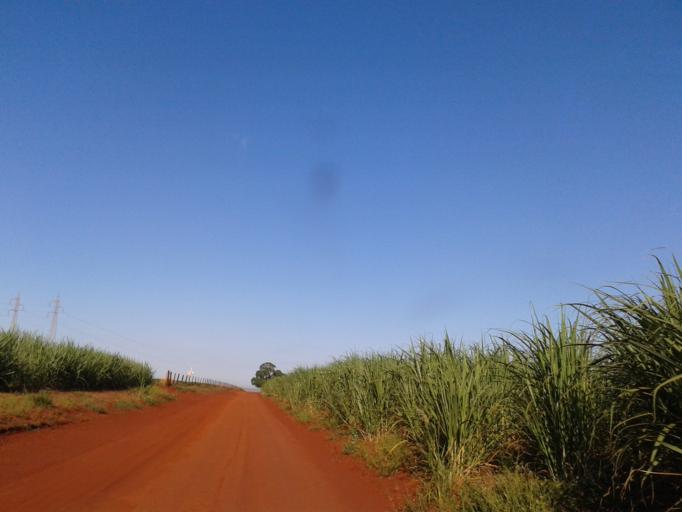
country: BR
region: Minas Gerais
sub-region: Centralina
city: Centralina
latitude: -18.6711
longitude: -49.2821
